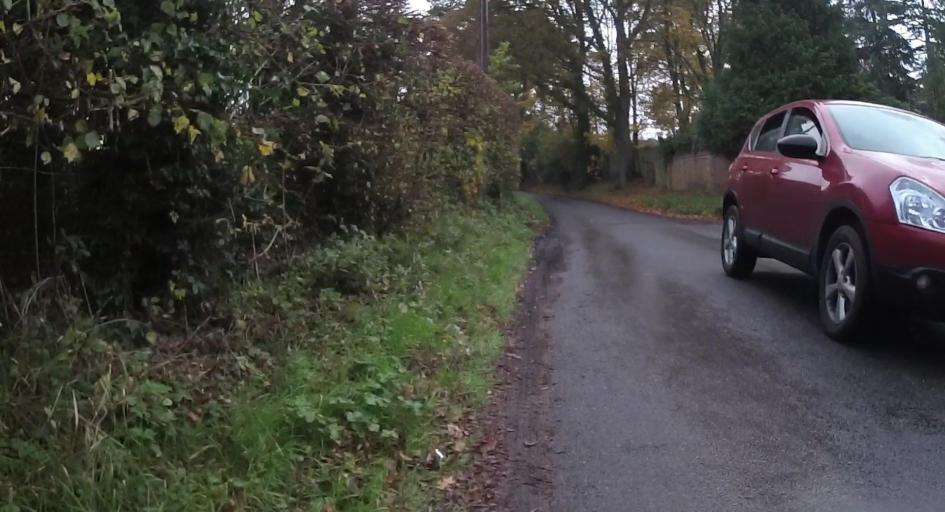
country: GB
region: England
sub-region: Wokingham
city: Finchampstead
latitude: 51.3677
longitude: -0.8608
